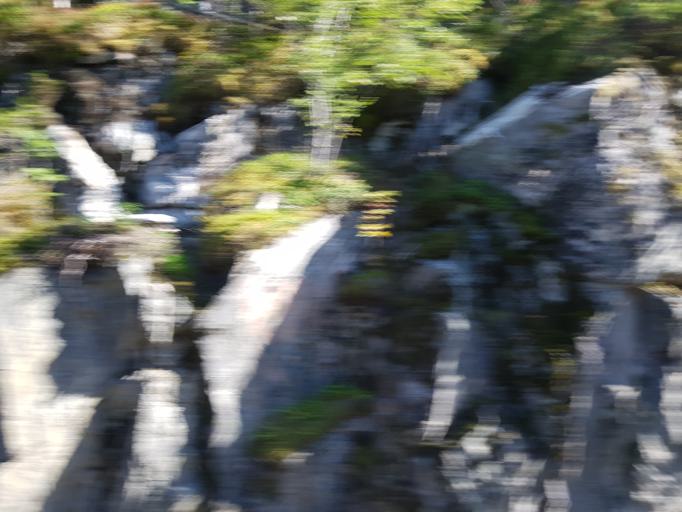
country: NO
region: Sor-Trondelag
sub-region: Afjord
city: A i Afjord
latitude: 63.7579
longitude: 10.2383
